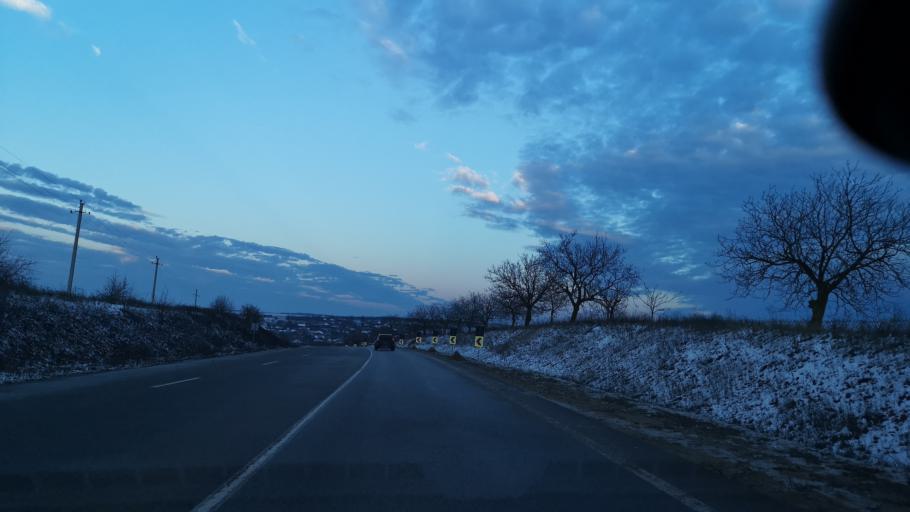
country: MD
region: Rezina
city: Saharna
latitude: 47.5846
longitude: 28.8162
